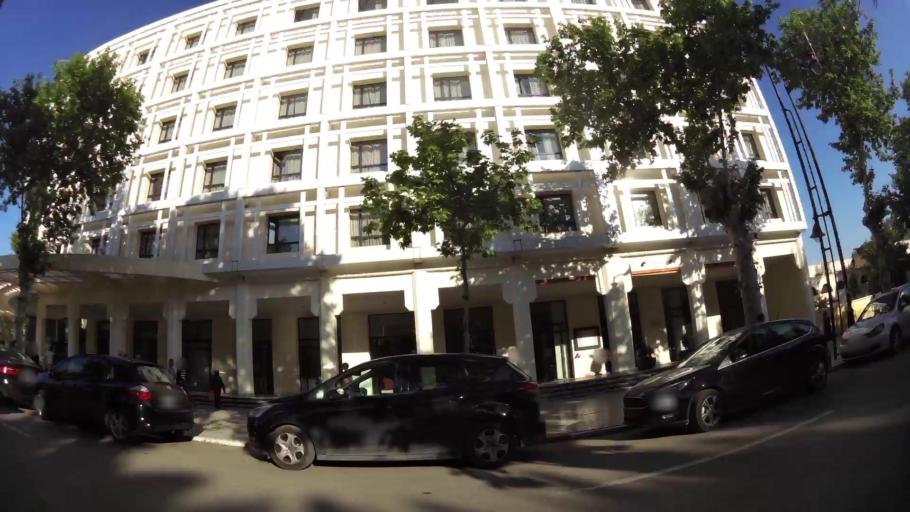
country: MA
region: Fes-Boulemane
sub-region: Fes
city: Fes
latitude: 34.0435
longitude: -4.9976
